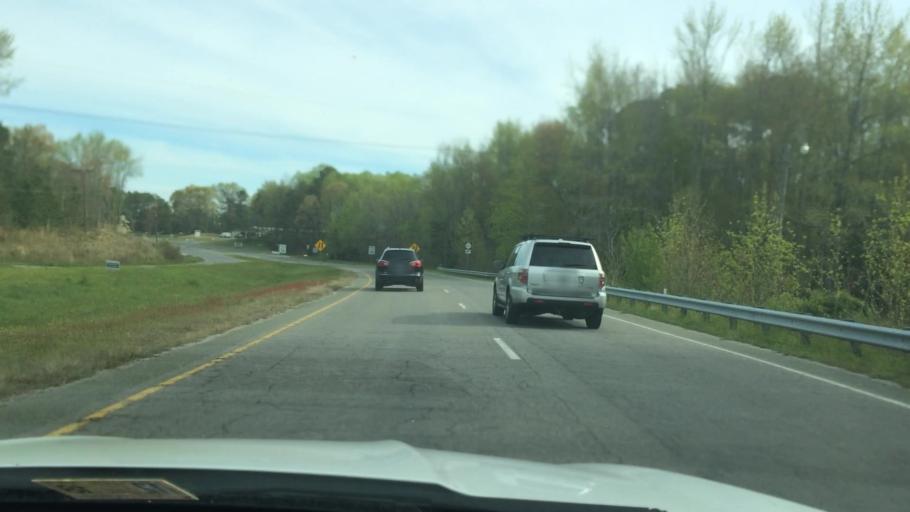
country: US
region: Virginia
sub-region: Lancaster County
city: Kilmarnock
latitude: 37.6966
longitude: -76.3738
